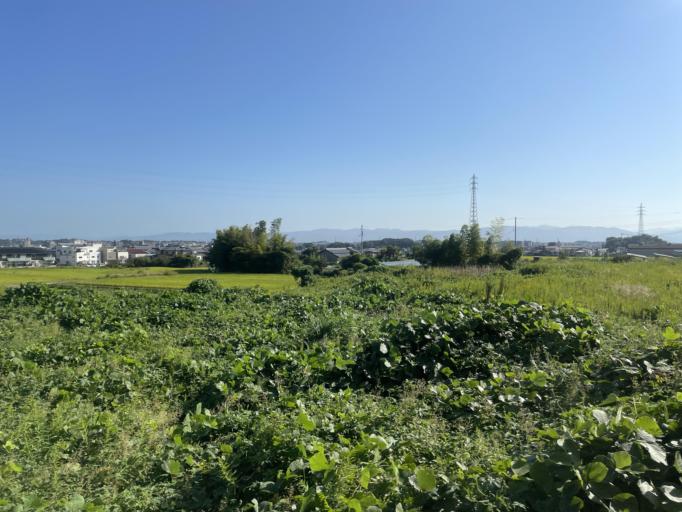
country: JP
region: Nara
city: Gose
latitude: 34.5295
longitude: 135.6962
